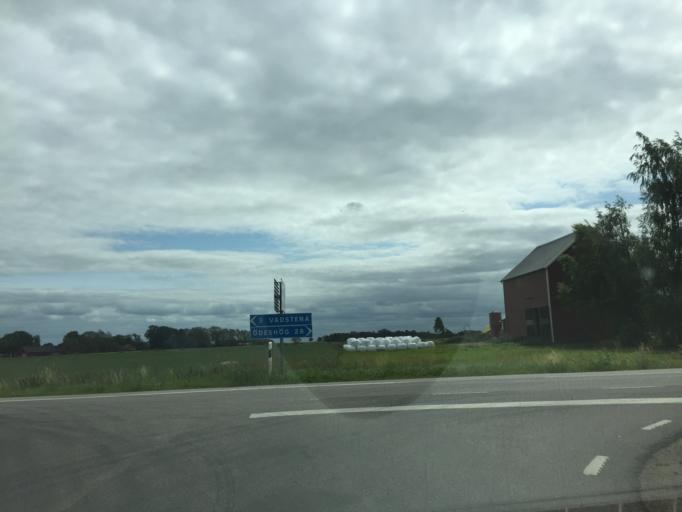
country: SE
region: OEstergoetland
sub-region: Vadstena Kommun
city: Vadstena
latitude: 58.4311
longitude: 14.8561
